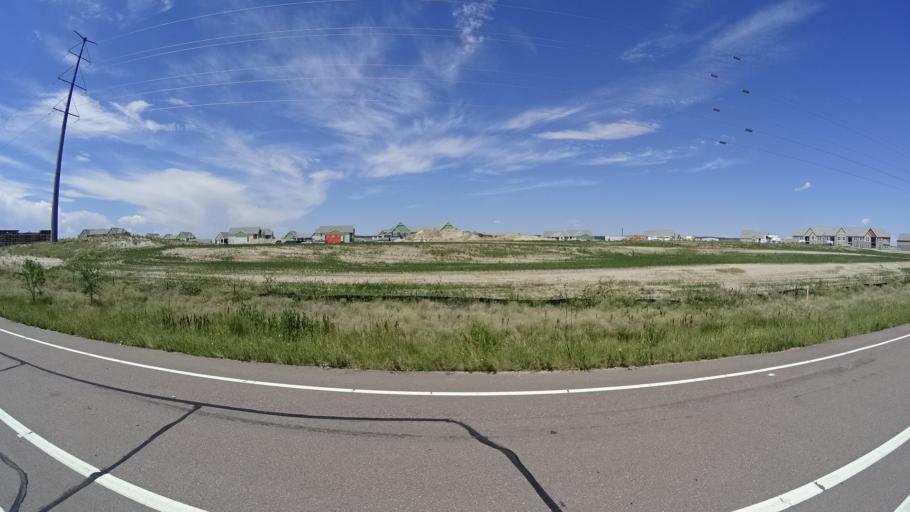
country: US
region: Colorado
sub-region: El Paso County
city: Black Forest
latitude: 38.9407
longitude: -104.7089
